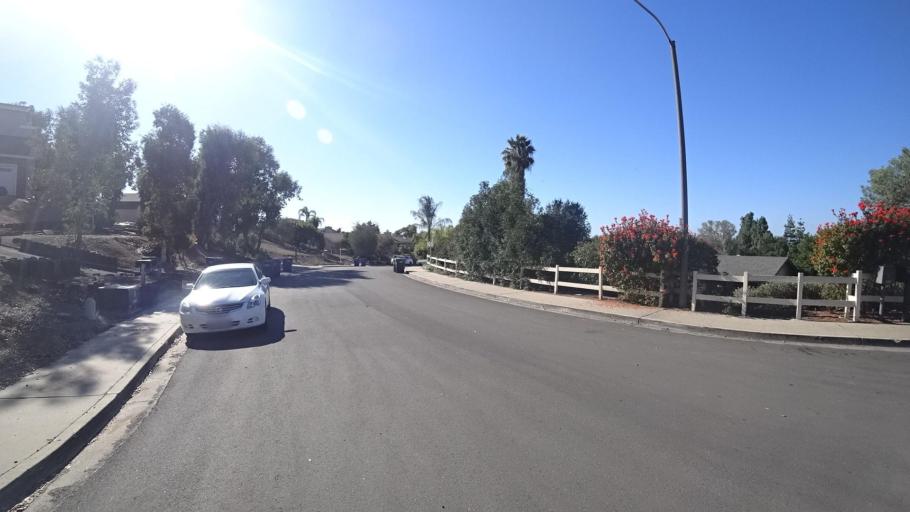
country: US
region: California
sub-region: San Diego County
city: Winter Gardens
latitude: 32.8284
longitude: -116.9273
